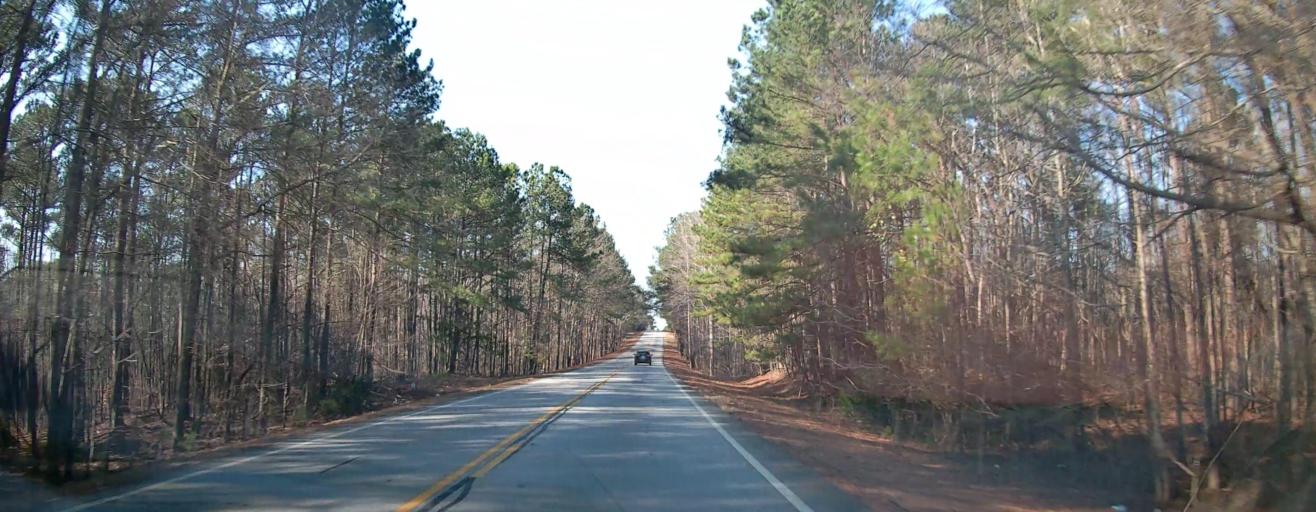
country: US
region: Georgia
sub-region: Butts County
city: Indian Springs
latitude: 33.2292
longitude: -83.8754
